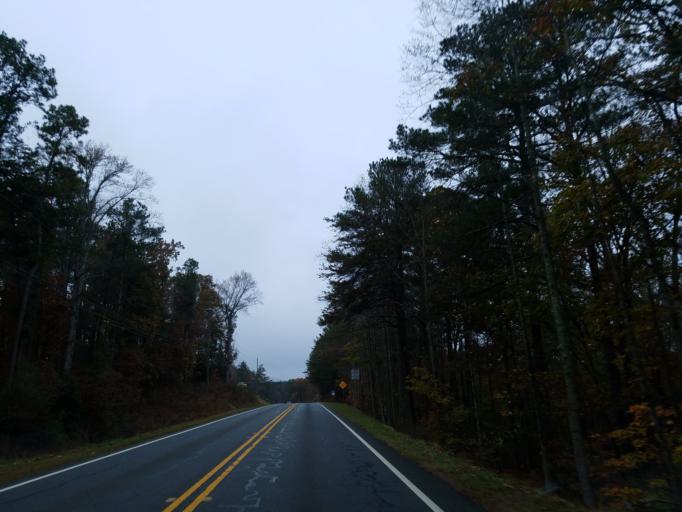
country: US
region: Georgia
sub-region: Pickens County
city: Jasper
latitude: 34.3833
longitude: -84.4742
